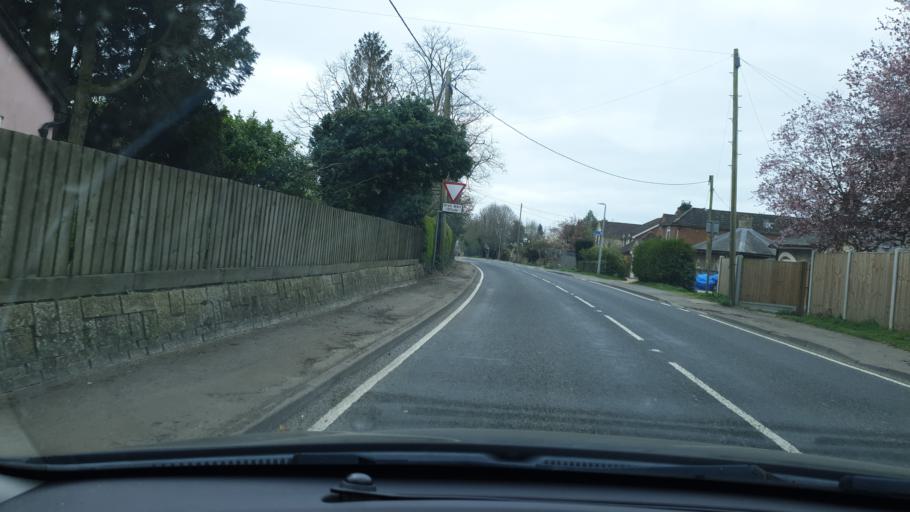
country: GB
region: England
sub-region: Essex
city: Great Horkesley
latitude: 51.9296
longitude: 0.8785
